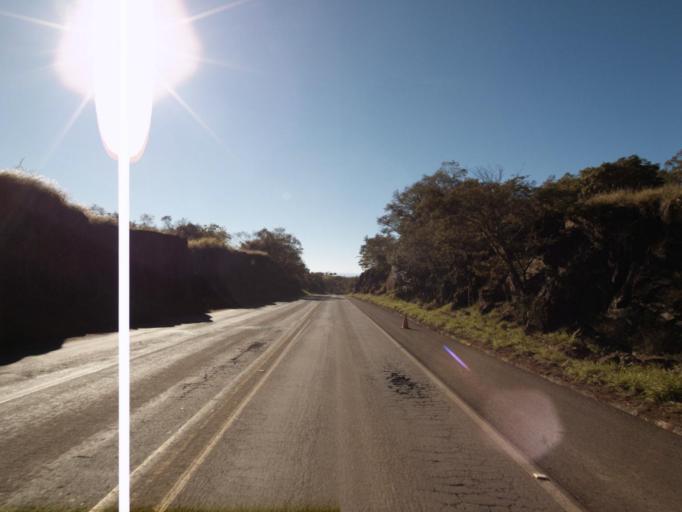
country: AR
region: Misiones
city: Bernardo de Irigoyen
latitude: -26.7659
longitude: -53.4905
